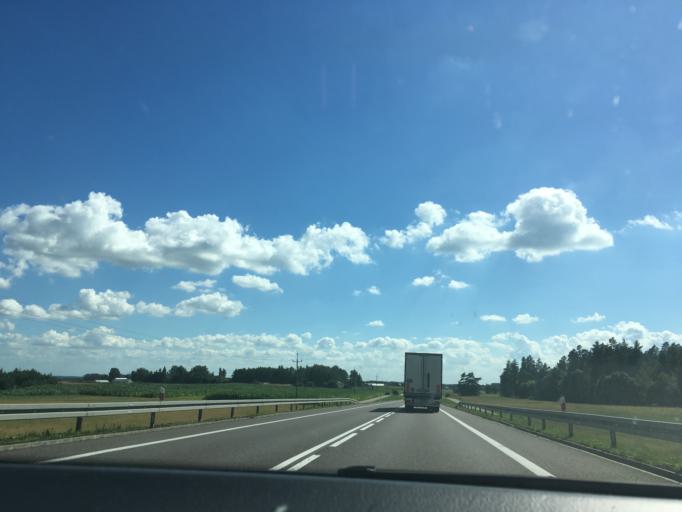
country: PL
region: Podlasie
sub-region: Powiat sokolski
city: Suchowola
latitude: 53.7202
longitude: 23.1053
